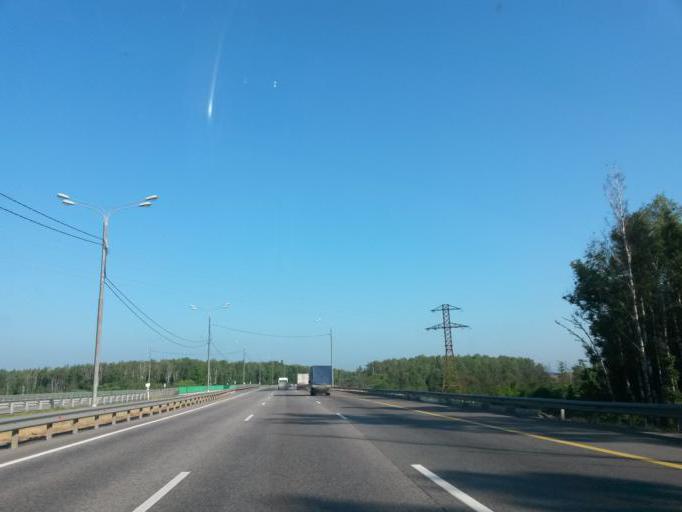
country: RU
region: Moskovskaya
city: Vostryakovo
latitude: 55.3625
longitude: 37.7909
